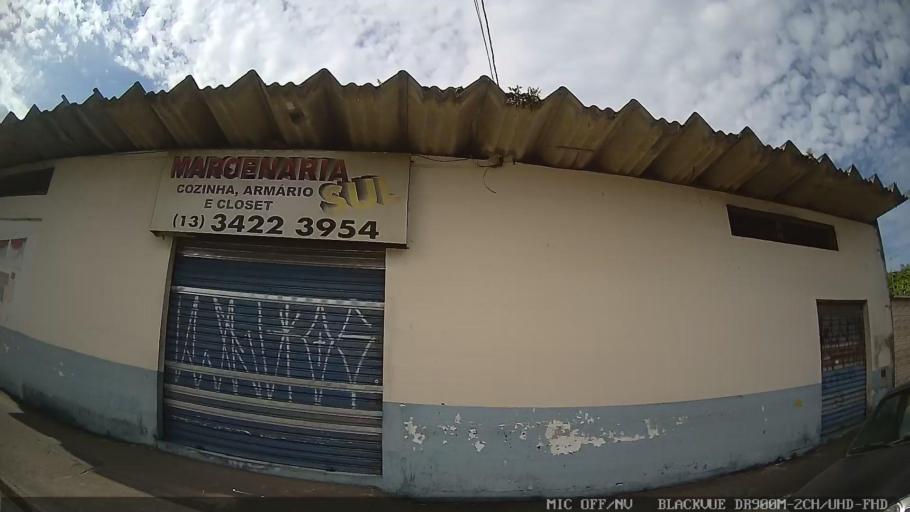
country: BR
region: Sao Paulo
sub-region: Itanhaem
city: Itanhaem
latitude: -24.1560
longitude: -46.7711
